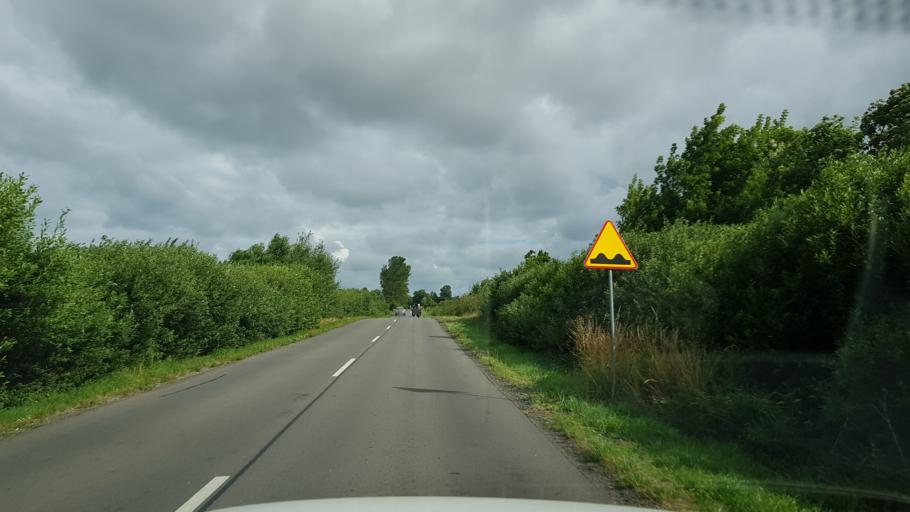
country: PL
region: West Pomeranian Voivodeship
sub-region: Powiat gryficki
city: Karnice
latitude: 54.0502
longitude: 15.0297
